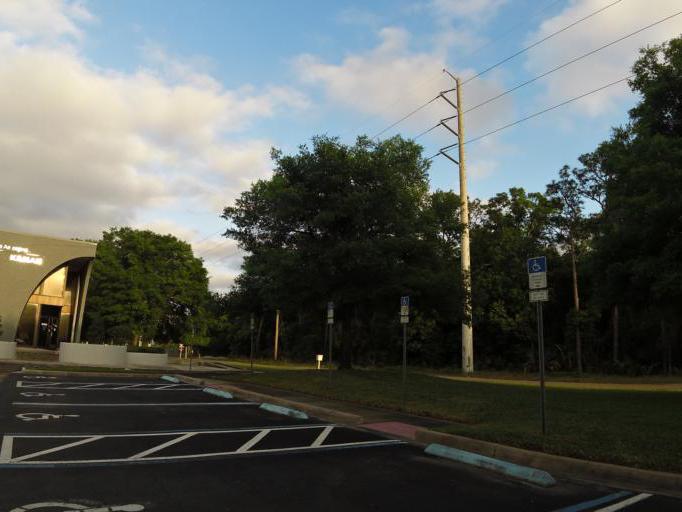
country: US
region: Florida
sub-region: Duval County
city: Jacksonville
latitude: 30.4103
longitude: -81.6460
